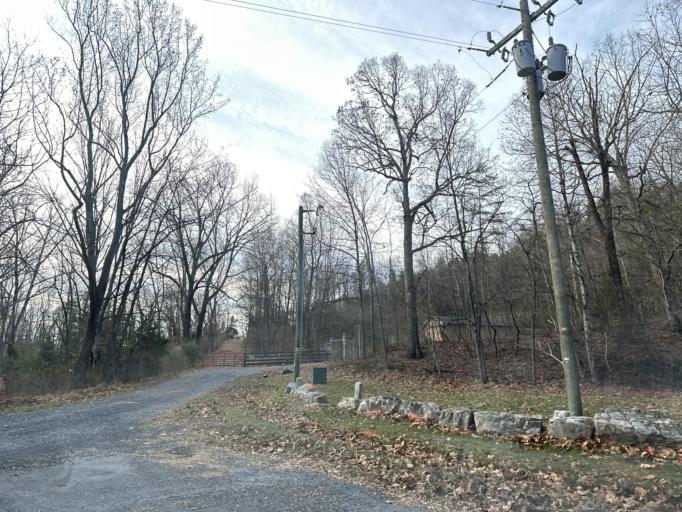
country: US
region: Virginia
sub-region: City of Staunton
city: Staunton
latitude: 38.2122
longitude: -79.2269
